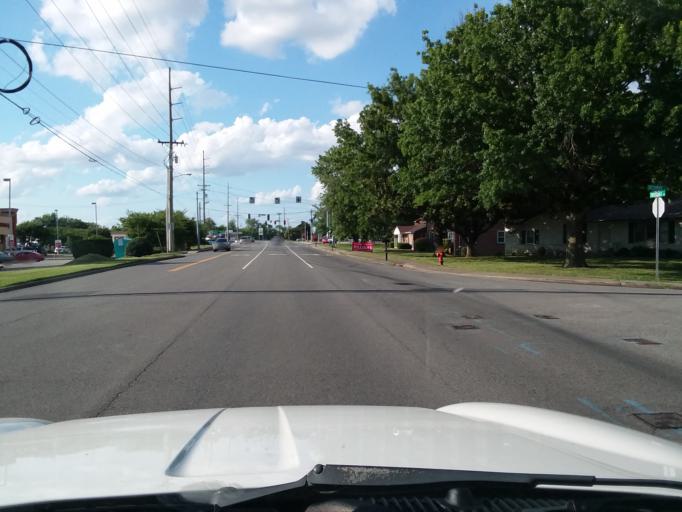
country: US
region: Tennessee
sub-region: Davidson County
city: Oak Hill
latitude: 36.0795
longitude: -86.7586
